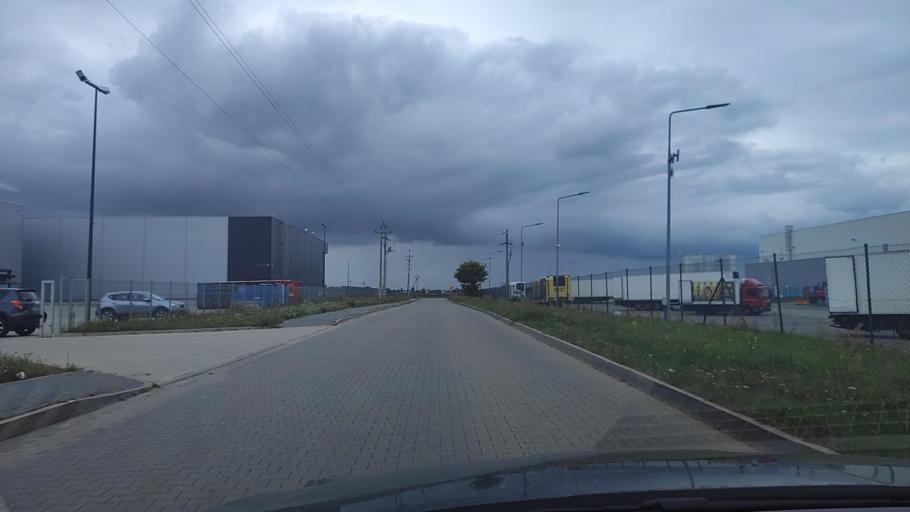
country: PL
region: Greater Poland Voivodeship
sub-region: Powiat poznanski
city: Kostrzyn
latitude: 52.3996
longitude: 17.2034
